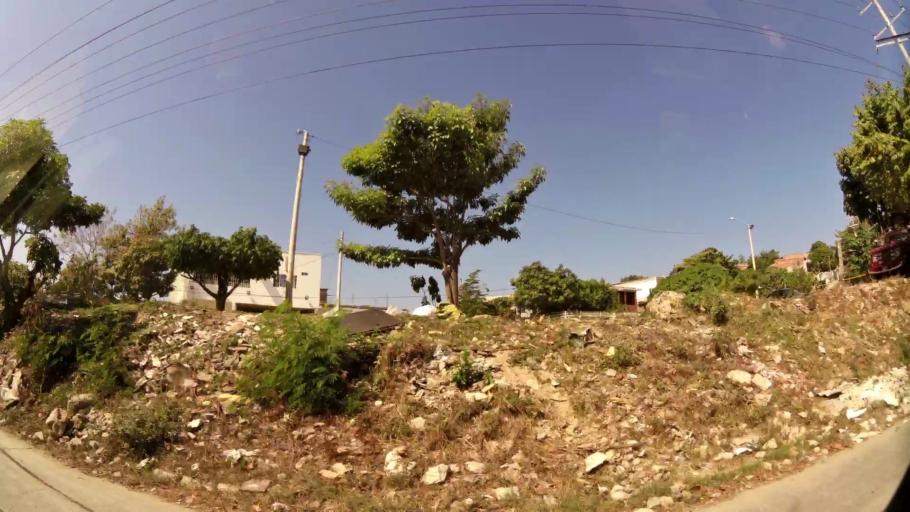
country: CO
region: Bolivar
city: Cartagena
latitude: 10.3933
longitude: -75.5074
